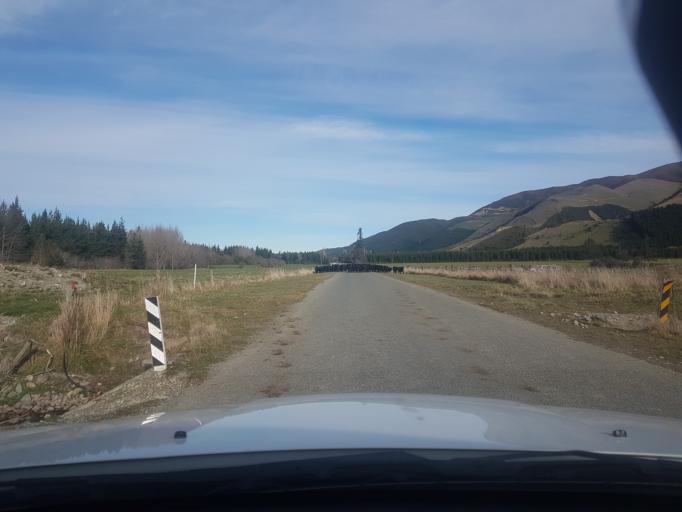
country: NZ
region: Canterbury
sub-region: Timaru District
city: Pleasant Point
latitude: -43.8412
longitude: 171.2540
